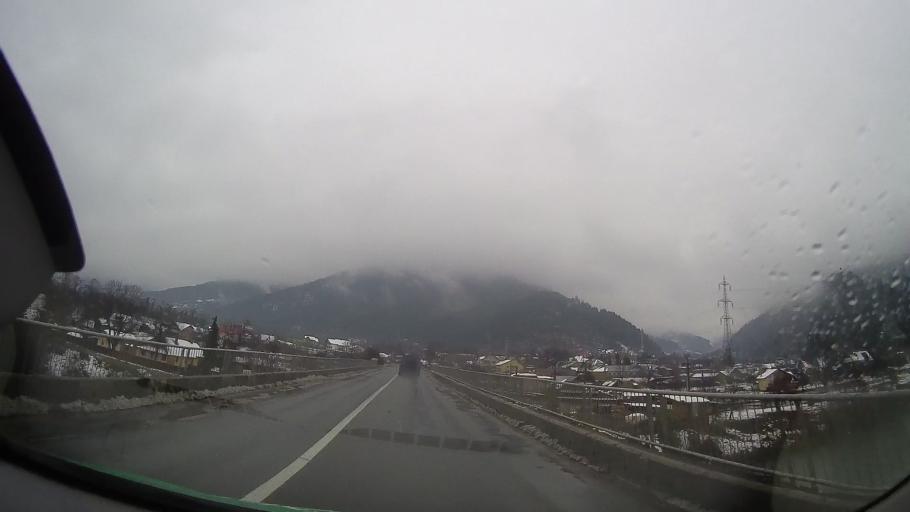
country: RO
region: Neamt
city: Viisoara
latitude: 46.9303
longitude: 26.2220
